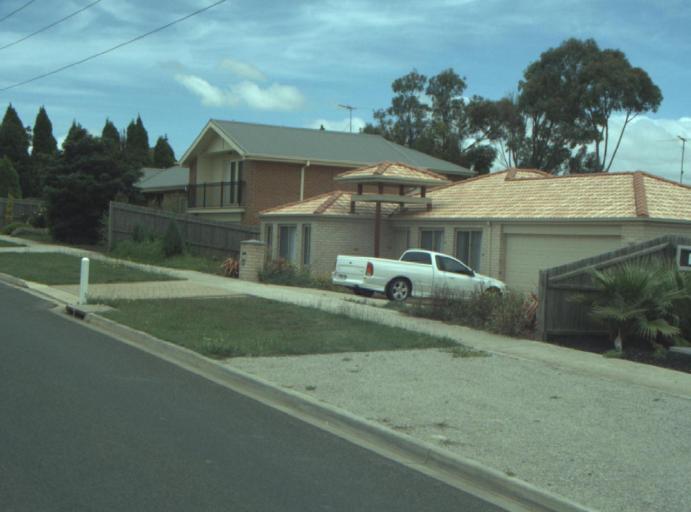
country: AU
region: Victoria
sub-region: Greater Geelong
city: Wandana Heights
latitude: -38.2095
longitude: 144.3023
